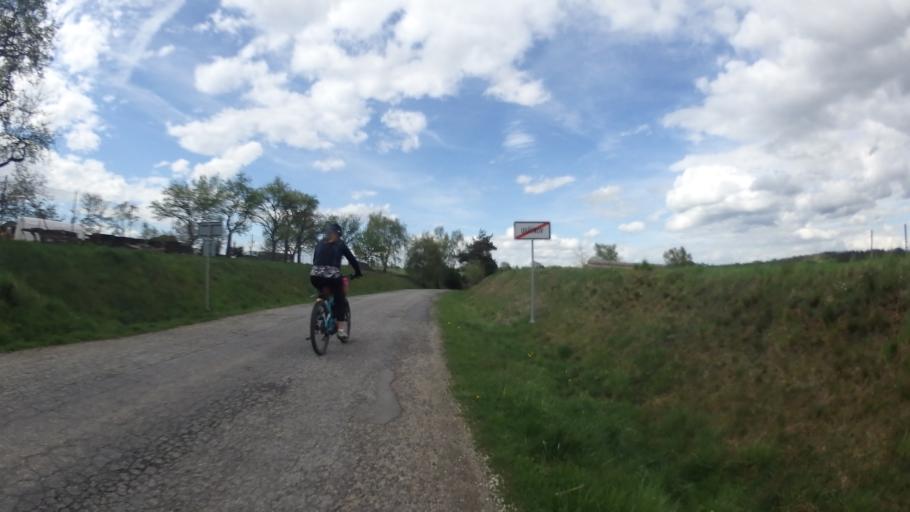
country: CZ
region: Vysocina
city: Merin
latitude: 49.3523
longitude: 15.9356
